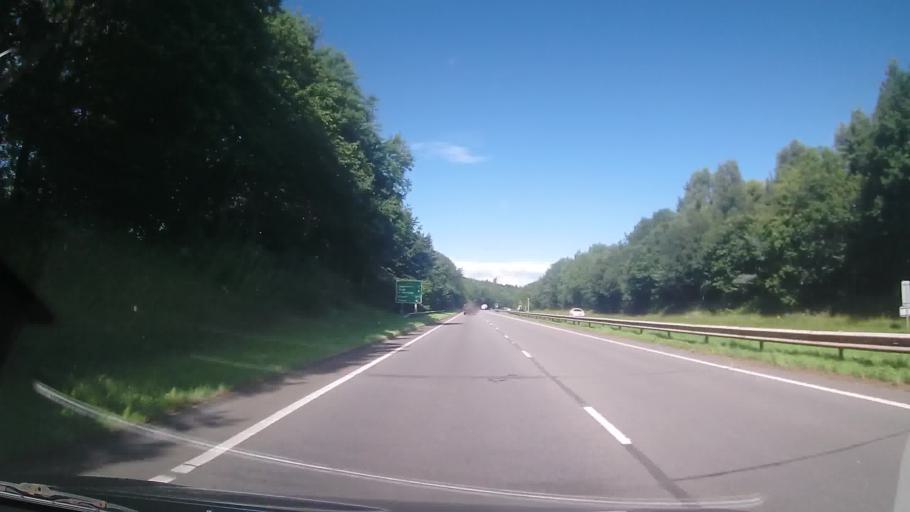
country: GB
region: Wales
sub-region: County of Flintshire
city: Hawarden
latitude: 53.1626
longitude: -3.0164
